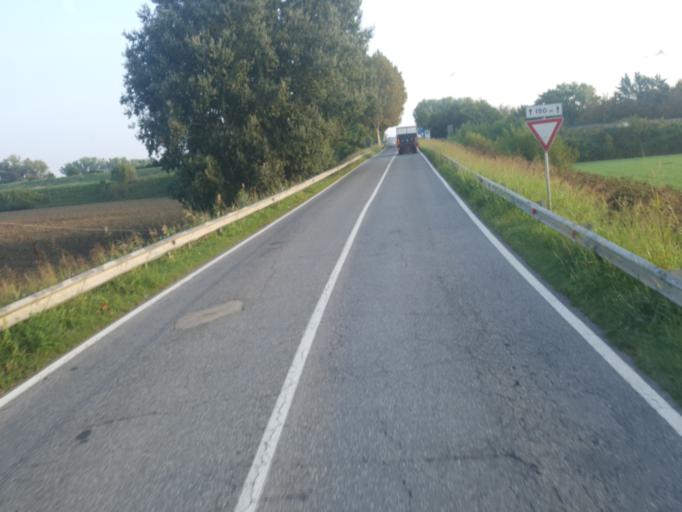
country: IT
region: Emilia-Romagna
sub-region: Provincia di Ferrara
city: San Biagio
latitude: 44.5746
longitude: 11.8739
